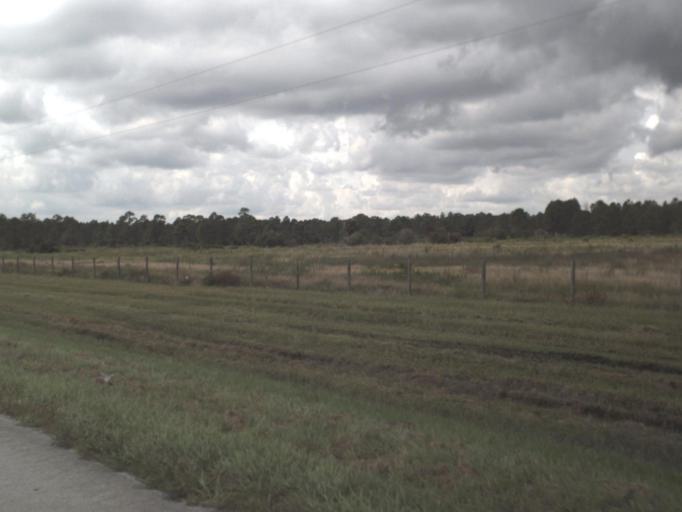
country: US
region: Florida
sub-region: Hendry County
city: Port LaBelle
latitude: 26.8989
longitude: -81.3382
